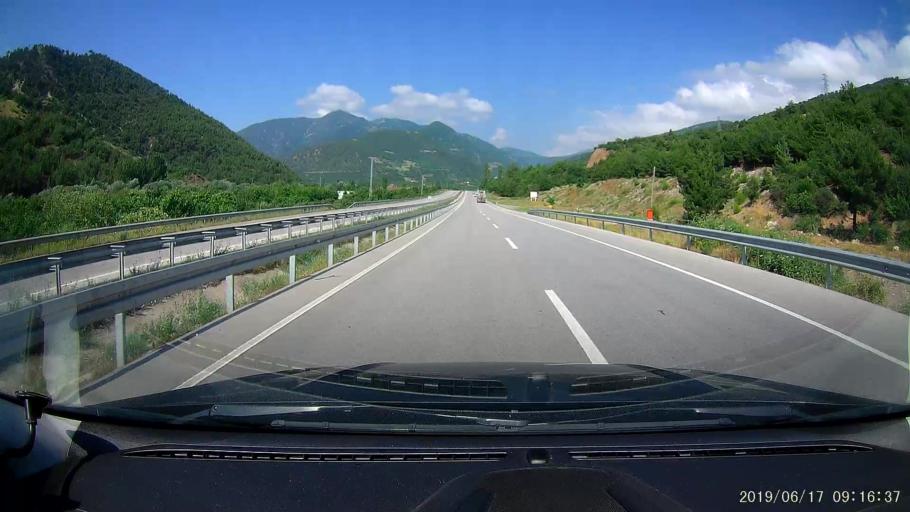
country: TR
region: Amasya
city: Akdag
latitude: 40.7442
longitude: 36.0071
